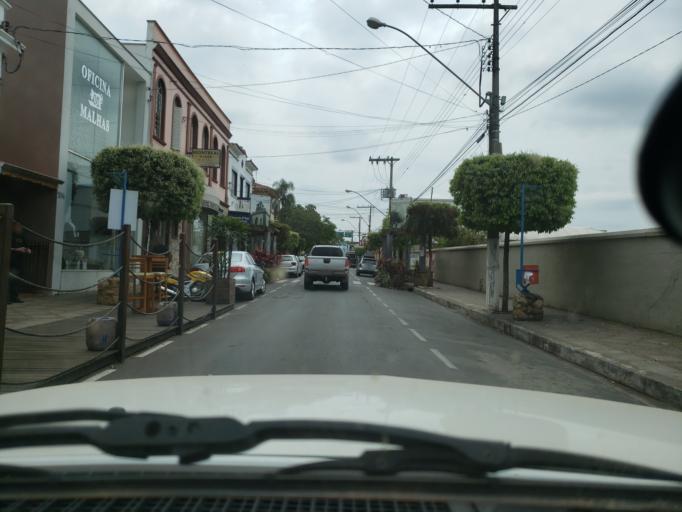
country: BR
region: Minas Gerais
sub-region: Jacutinga
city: Jacutinga
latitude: -22.2869
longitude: -46.6125
